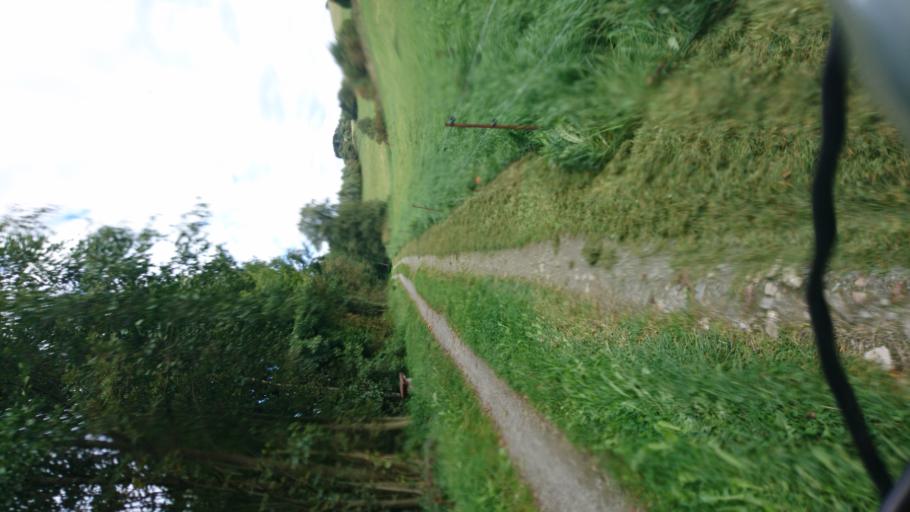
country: DE
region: Saxony
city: Konigswalde
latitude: 50.5705
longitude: 13.0541
